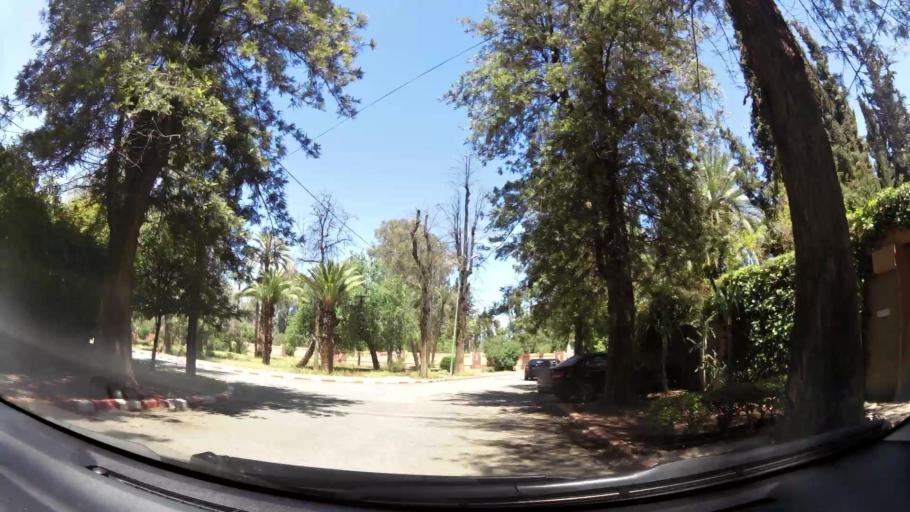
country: MA
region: Marrakech-Tensift-Al Haouz
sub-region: Marrakech
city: Marrakesh
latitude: 31.6237
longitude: -8.0101
